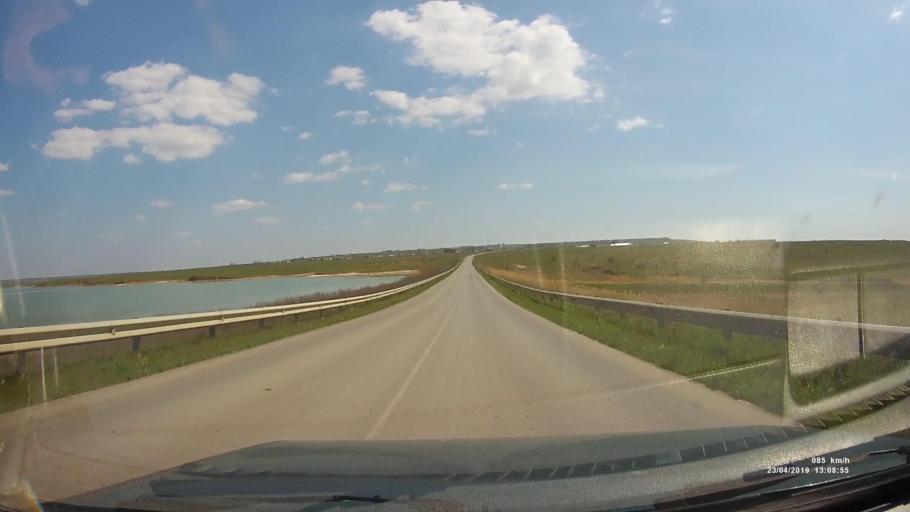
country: RU
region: Kalmykiya
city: Yashalta
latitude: 46.5795
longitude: 42.7820
